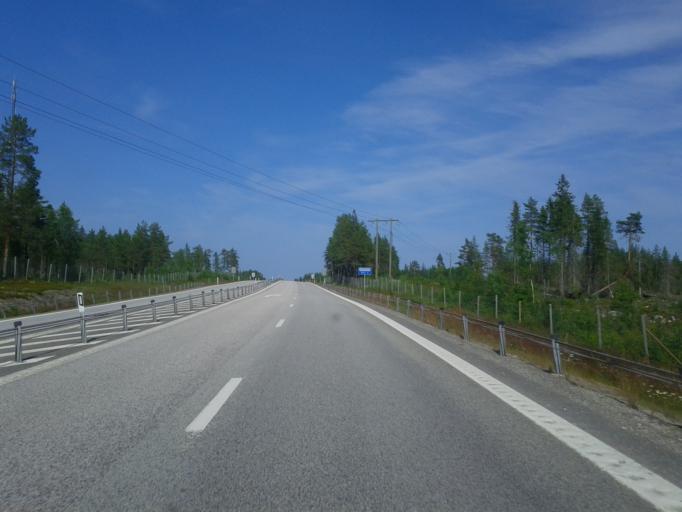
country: SE
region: Vaesterbotten
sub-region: Umea Kommun
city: Hoernefors
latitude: 63.6496
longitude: 19.9467
